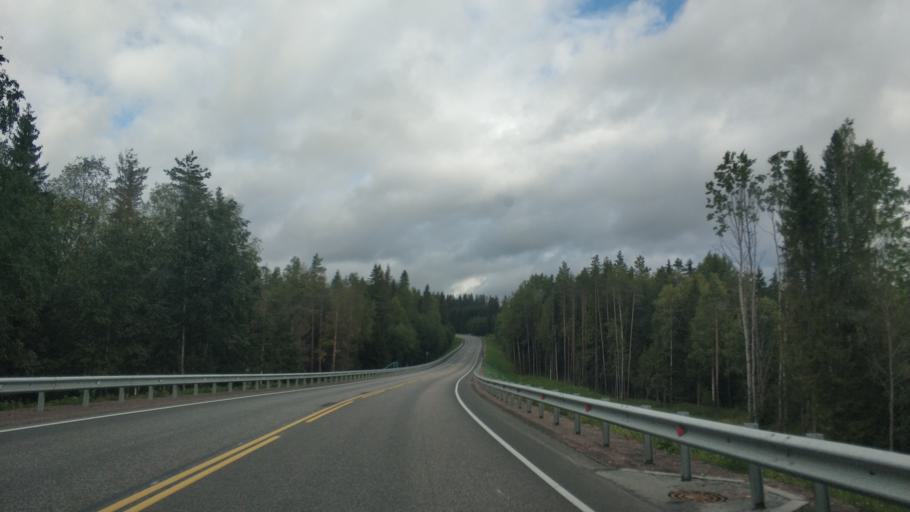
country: RU
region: Republic of Karelia
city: Khelyulya
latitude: 61.7883
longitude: 30.6336
